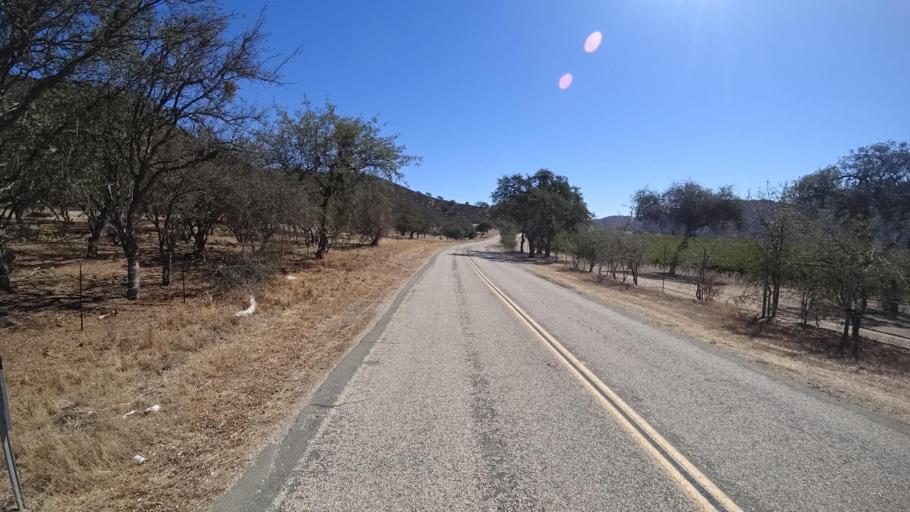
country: US
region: California
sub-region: Monterey County
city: Greenfield
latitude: 36.2703
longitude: -121.3842
